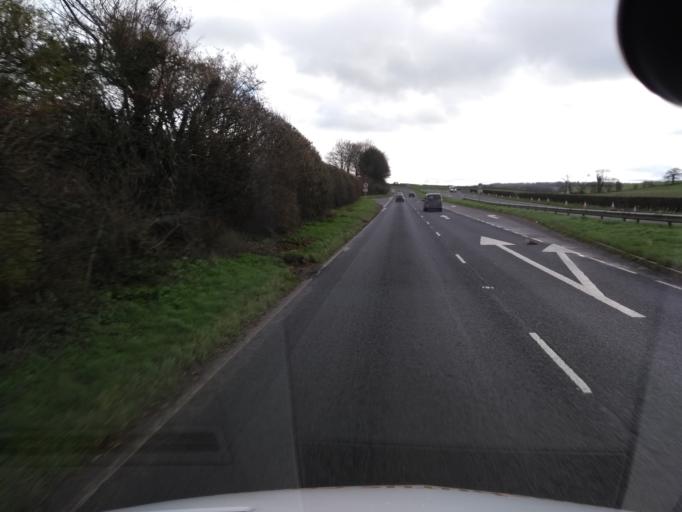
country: GB
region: England
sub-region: Dorset
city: Sherborne
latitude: 50.9452
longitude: -2.5622
